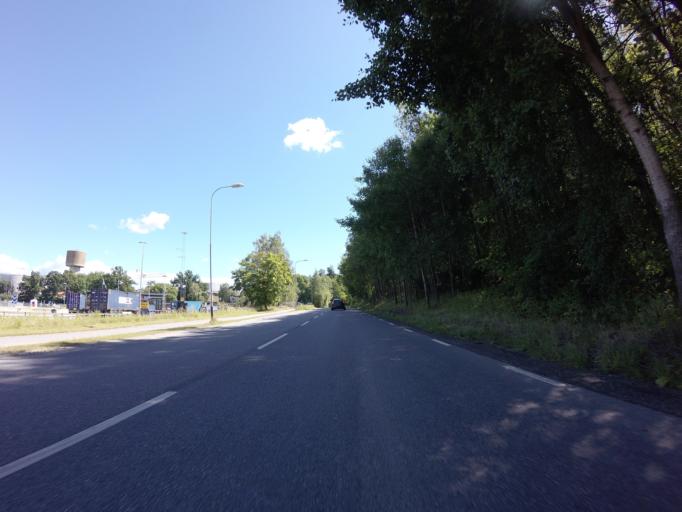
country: SE
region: Stockholm
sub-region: Lidingo
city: Lidingoe
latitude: 59.3388
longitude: 18.1286
